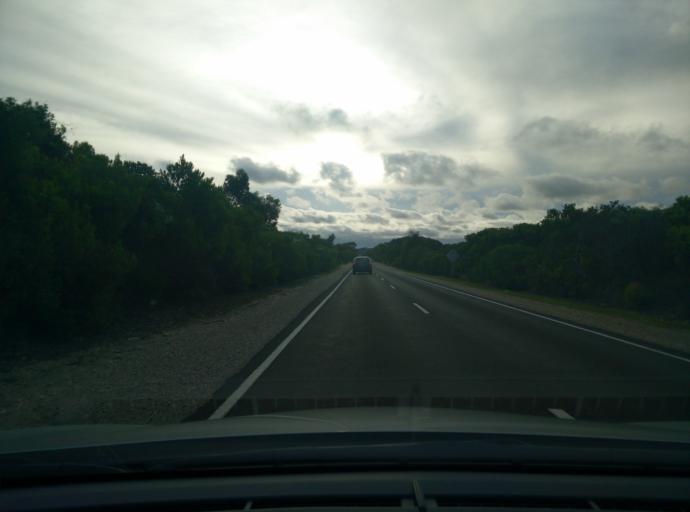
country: AU
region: South Australia
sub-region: Kangaroo Island
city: Kingscote
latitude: -35.8367
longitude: 137.7857
